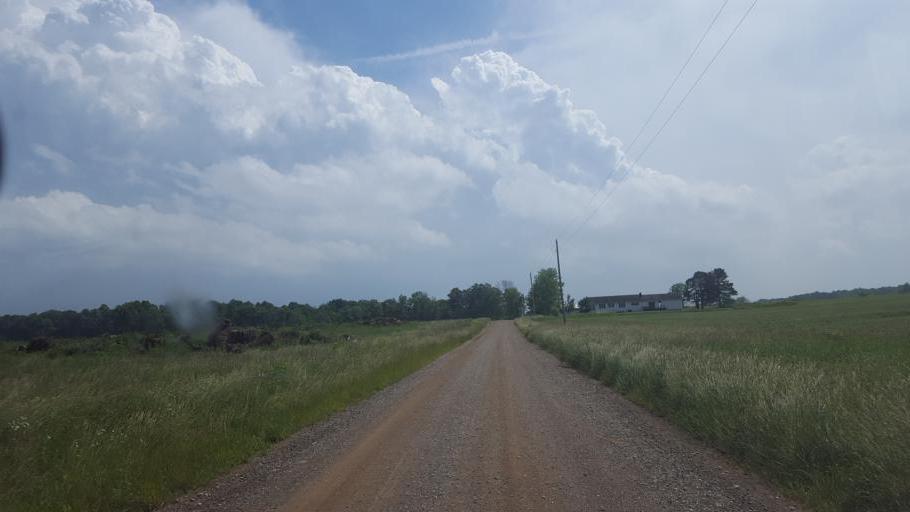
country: US
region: Ohio
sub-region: Knox County
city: Oak Hill
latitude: 40.3237
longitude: -82.2396
